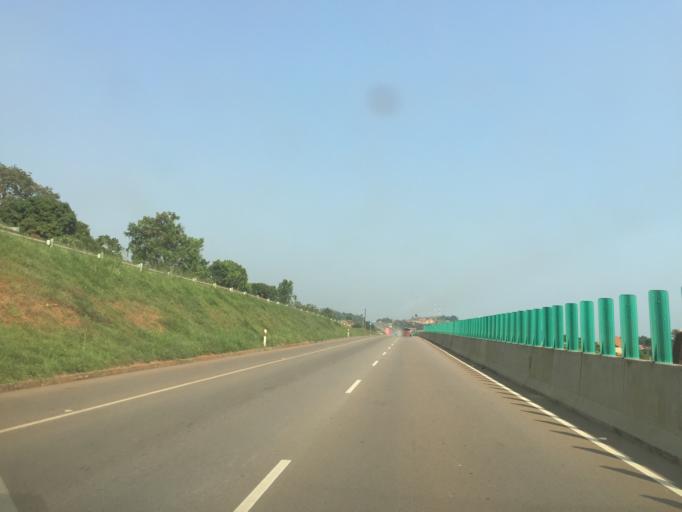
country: UG
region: Central Region
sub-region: Wakiso District
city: Kajansi
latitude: 0.2099
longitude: 32.5610
